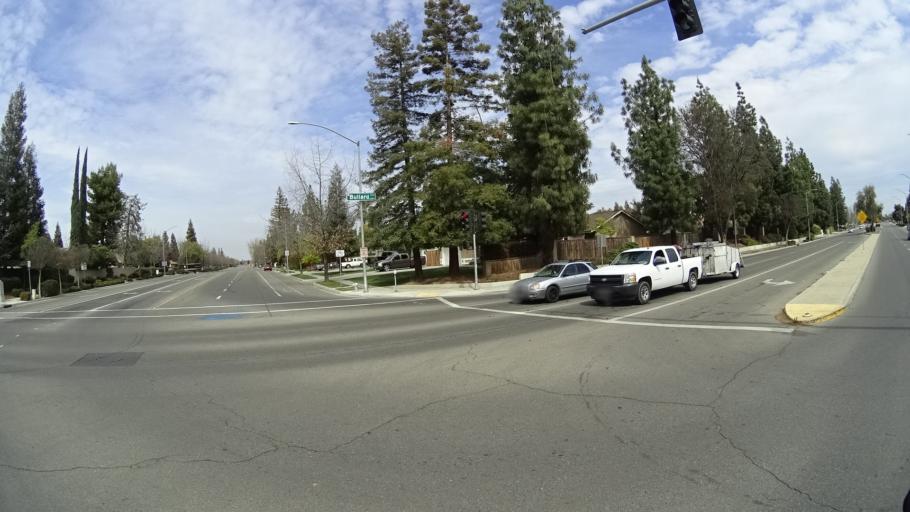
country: US
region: California
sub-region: Fresno County
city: West Park
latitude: 36.8221
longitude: -119.8745
